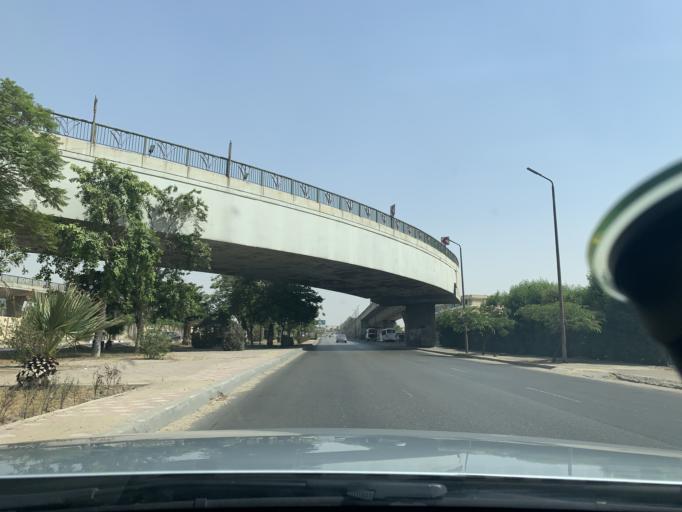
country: EG
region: Muhafazat al Qalyubiyah
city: Al Khankah
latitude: 30.1102
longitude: 31.3837
